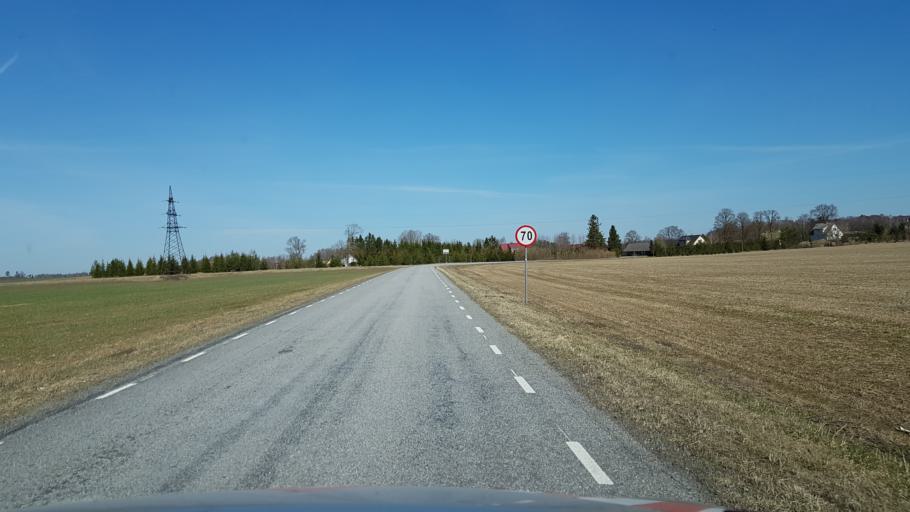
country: EE
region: Laeaene-Virumaa
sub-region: Vinni vald
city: Vinni
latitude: 59.2867
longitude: 26.3852
